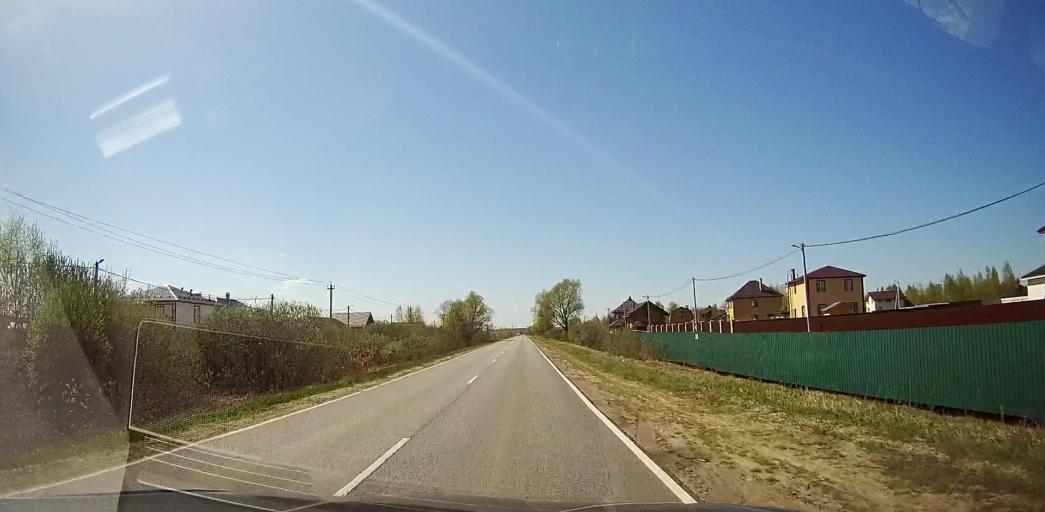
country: RU
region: Moskovskaya
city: Bronnitsy
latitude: 55.4561
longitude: 38.2790
